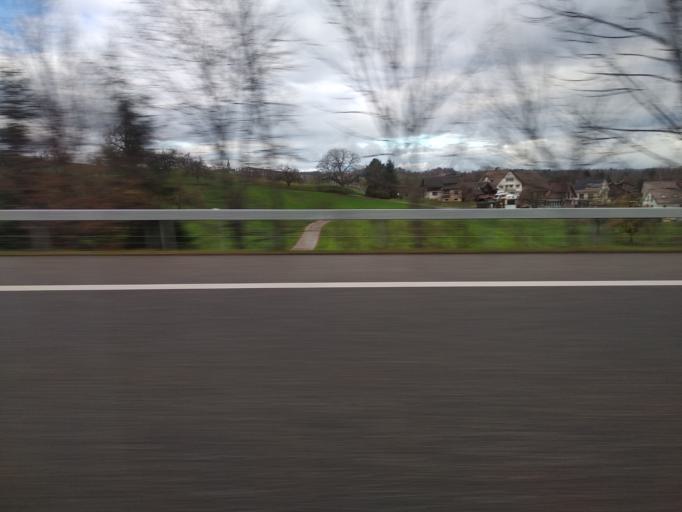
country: CH
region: Saint Gallen
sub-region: Wahlkreis Rorschach
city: Morschwil
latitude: 47.4652
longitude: 9.4394
